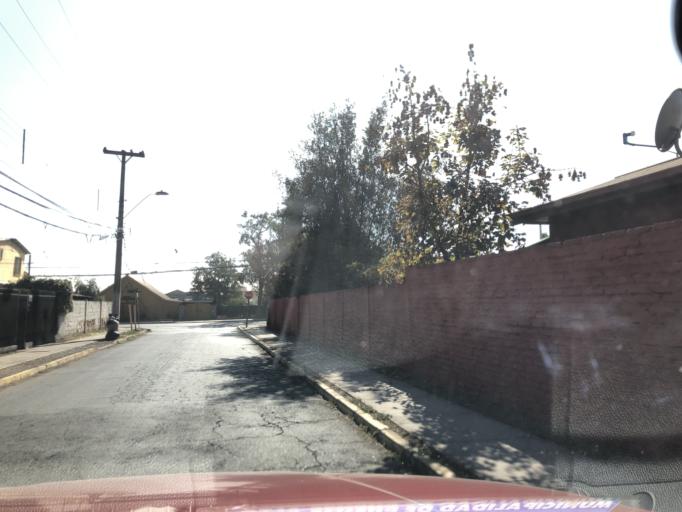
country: CL
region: Santiago Metropolitan
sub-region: Provincia de Cordillera
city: Puente Alto
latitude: -33.5629
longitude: -70.5776
